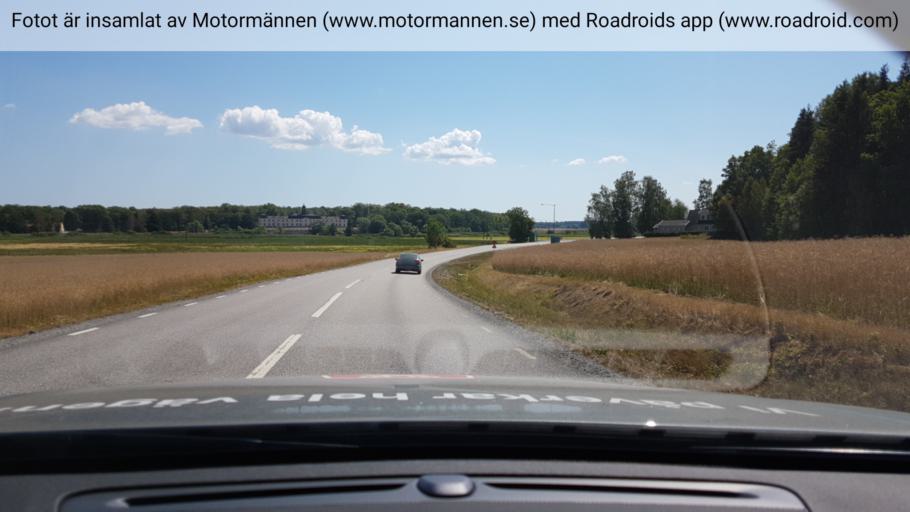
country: SE
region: Stockholm
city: Stenhamra
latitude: 59.3665
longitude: 17.7171
